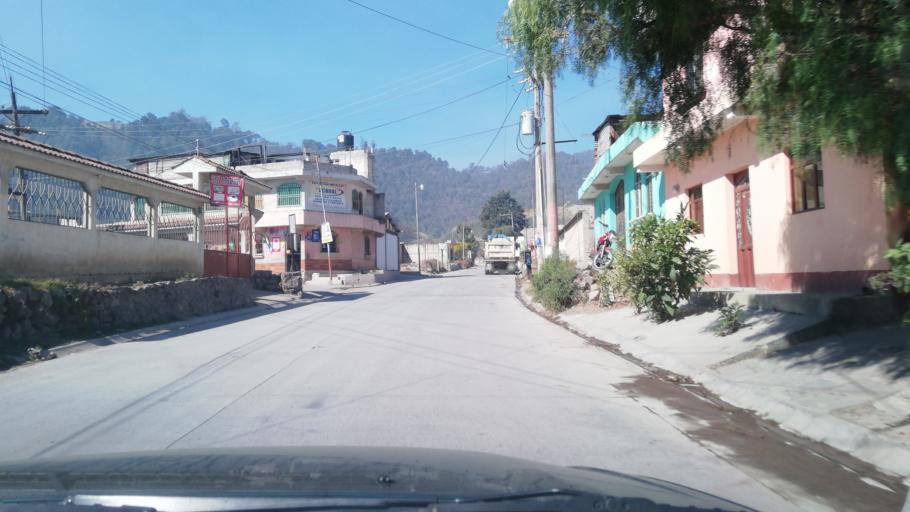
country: GT
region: Quetzaltenango
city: Quetzaltenango
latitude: 14.8067
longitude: -91.5531
